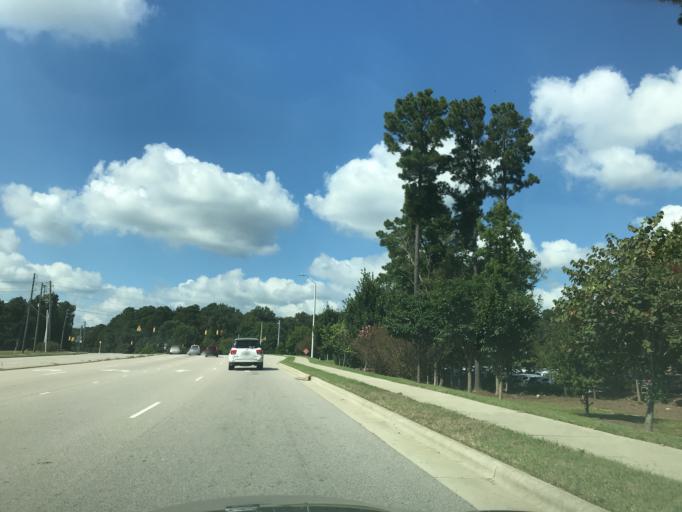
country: US
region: North Carolina
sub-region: Wake County
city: Wake Forest
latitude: 35.8920
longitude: -78.5580
